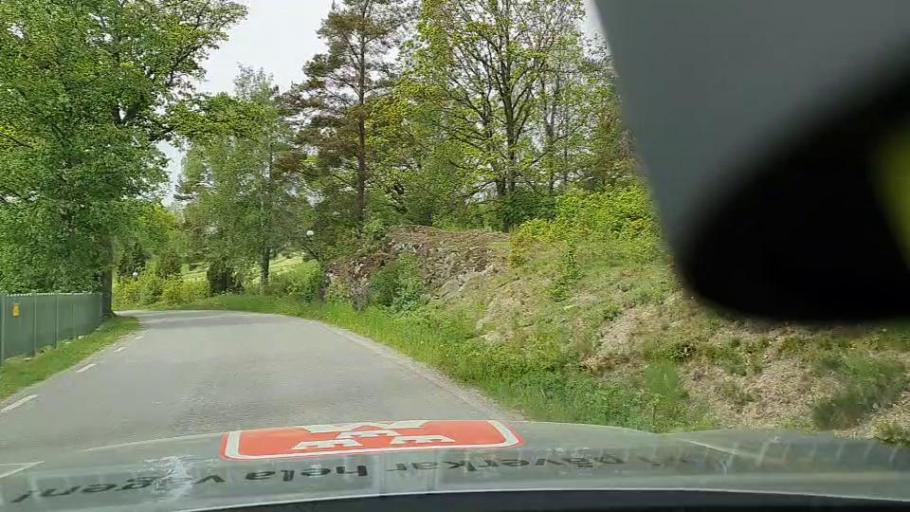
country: SE
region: Soedermanland
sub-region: Flens Kommun
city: Halleforsnas
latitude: 59.1004
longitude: 16.4835
